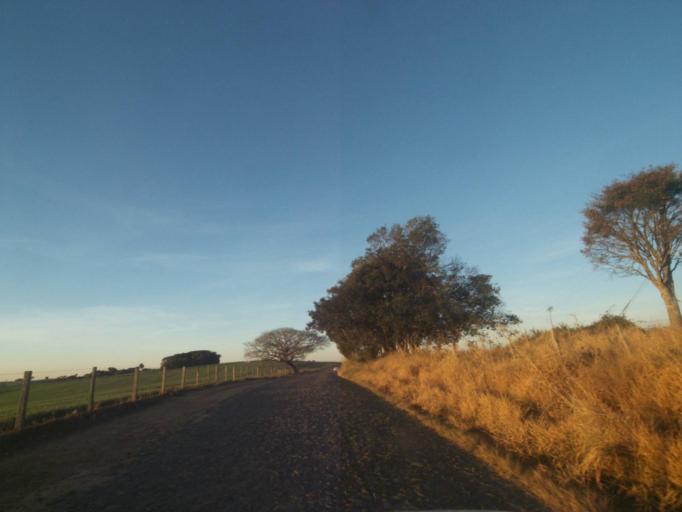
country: BR
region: Parana
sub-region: Tibagi
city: Tibagi
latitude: -24.5287
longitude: -50.4568
